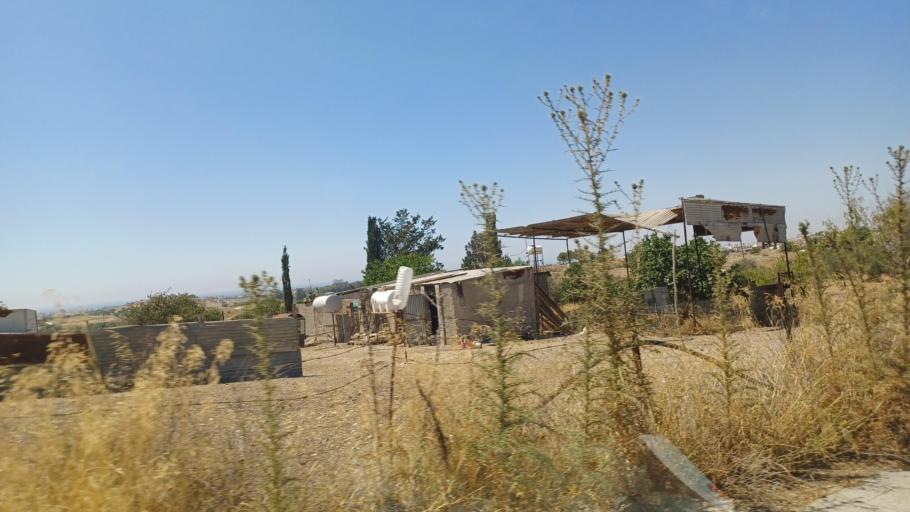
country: CY
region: Larnaka
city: Voroklini
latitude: 34.9996
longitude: 33.6639
